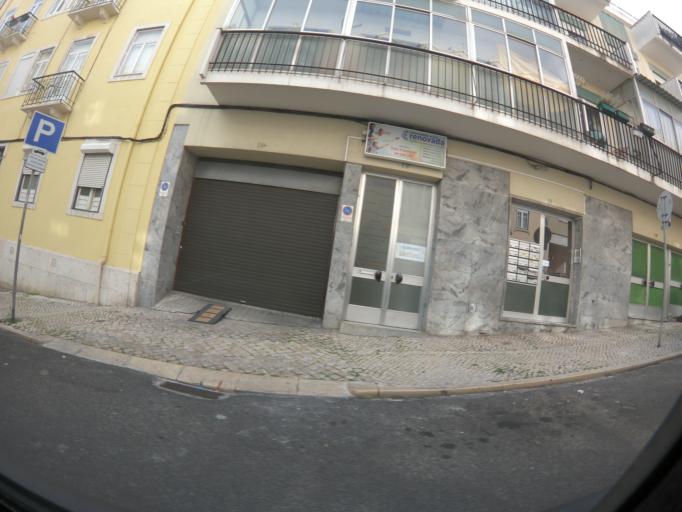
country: PT
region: Lisbon
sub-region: Lisbon
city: Lisbon
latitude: 38.7331
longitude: -9.1364
